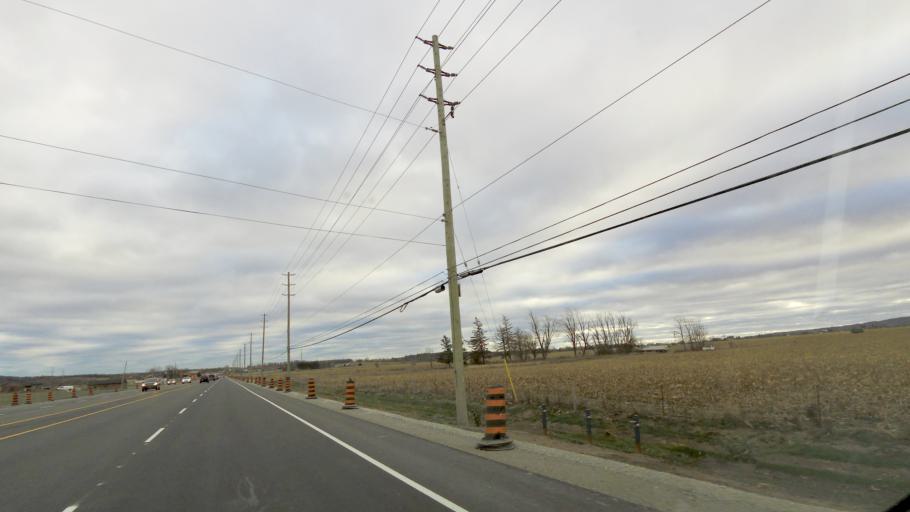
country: CA
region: Ontario
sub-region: Halton
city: Milton
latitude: 43.4731
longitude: -79.8160
